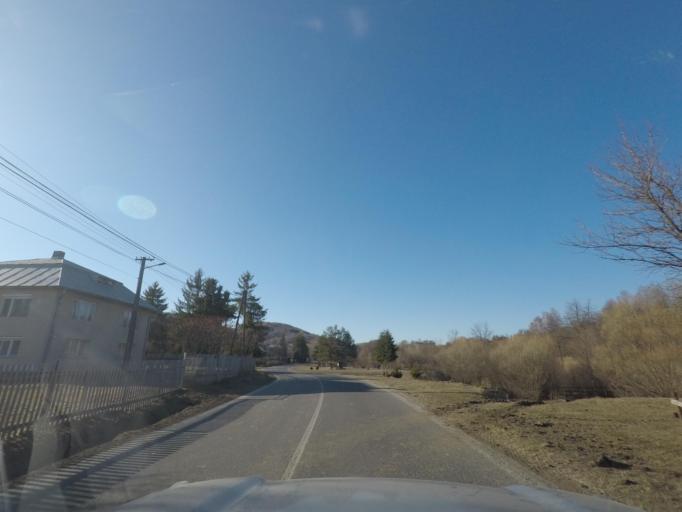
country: SK
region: Presovsky
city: Medzilaborce
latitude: 49.1978
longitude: 21.9972
